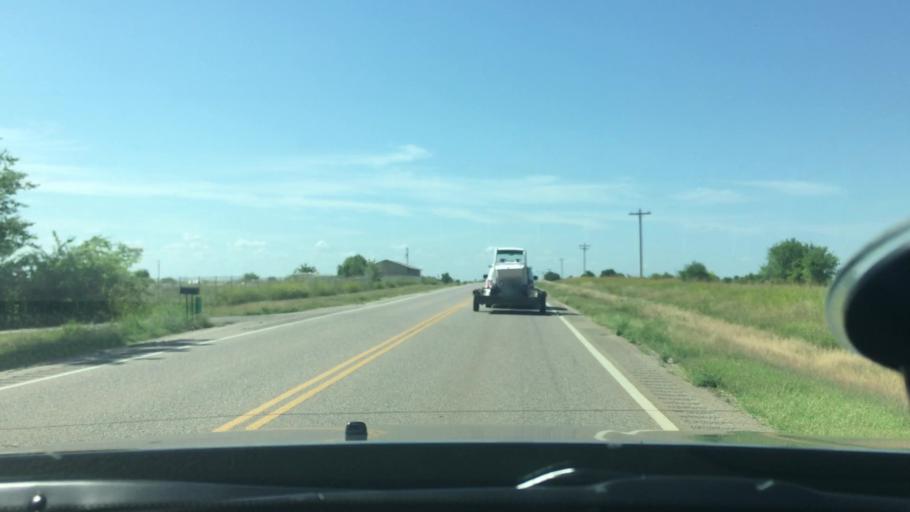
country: US
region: Oklahoma
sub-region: Marshall County
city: Kingston
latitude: 34.0324
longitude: -96.7611
